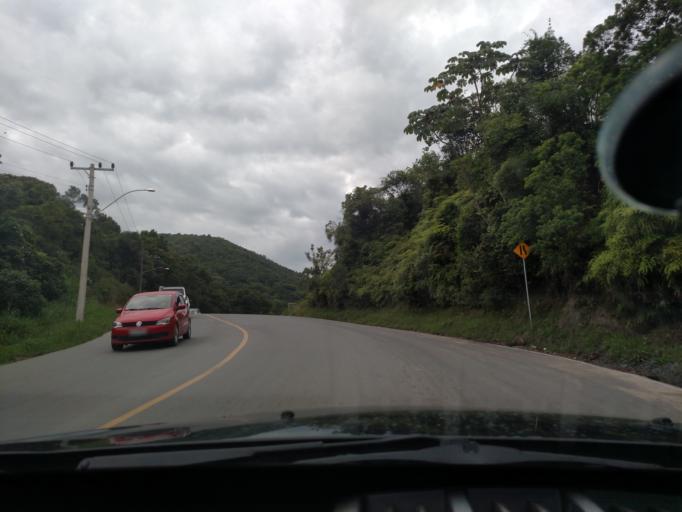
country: BR
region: Santa Catarina
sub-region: Porto Belo
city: Porto Belo
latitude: -27.1565
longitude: -48.5149
